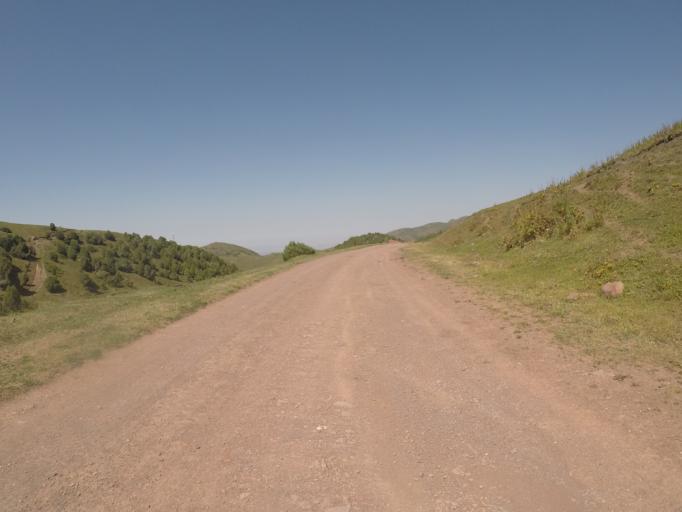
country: KG
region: Chuy
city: Bishkek
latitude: 42.6460
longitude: 74.5633
